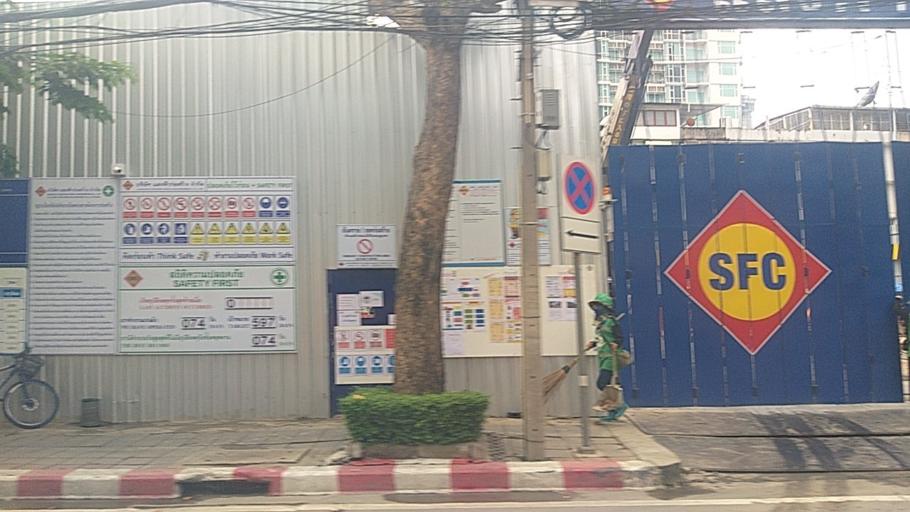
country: TH
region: Bangkok
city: Bang Rak
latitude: 13.7313
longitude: 100.5229
